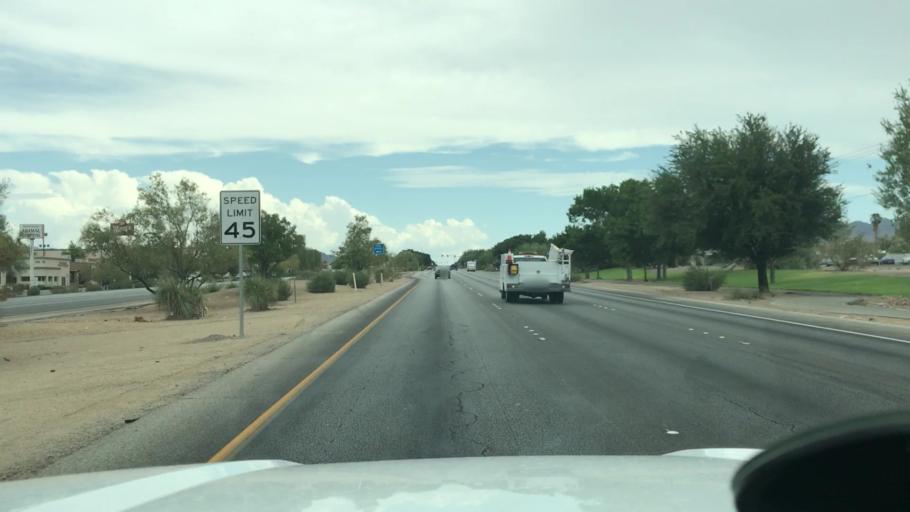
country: US
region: Nevada
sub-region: Clark County
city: Henderson
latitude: 36.0359
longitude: -114.9781
